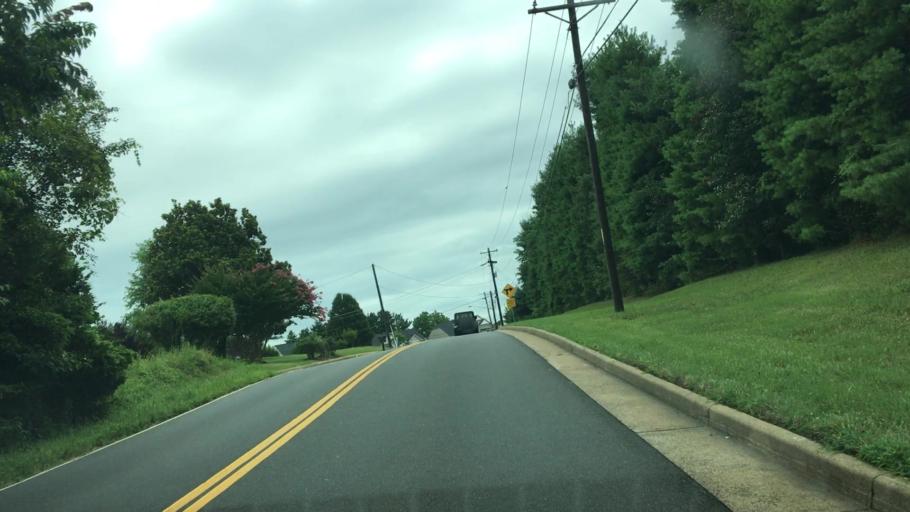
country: US
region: Virginia
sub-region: Prince William County
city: Buckhall
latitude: 38.7483
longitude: -77.4425
